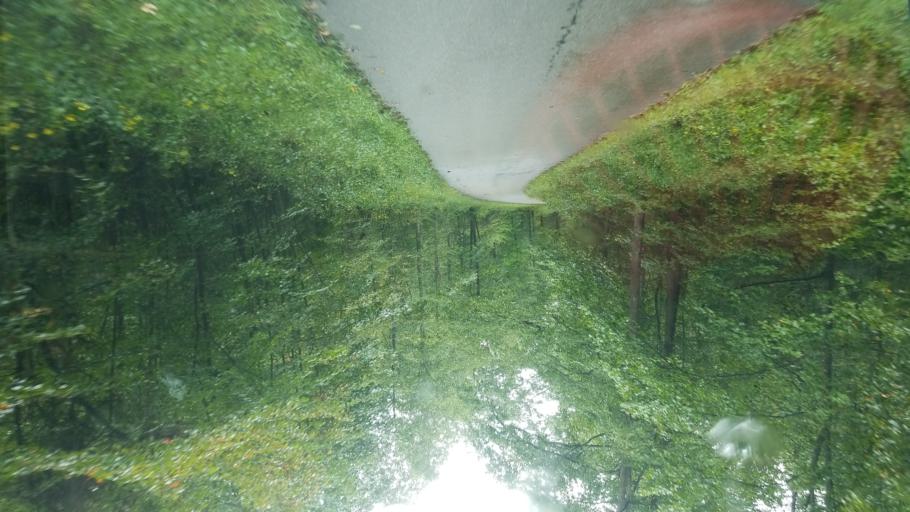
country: US
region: Ohio
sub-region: Scioto County
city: West Portsmouth
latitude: 38.7722
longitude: -83.1411
